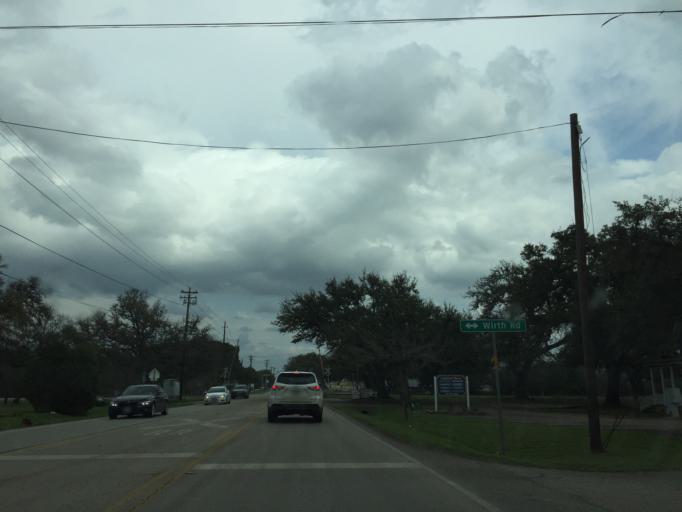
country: US
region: Texas
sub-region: Travis County
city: Manchaca
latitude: 30.1405
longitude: -97.8312
